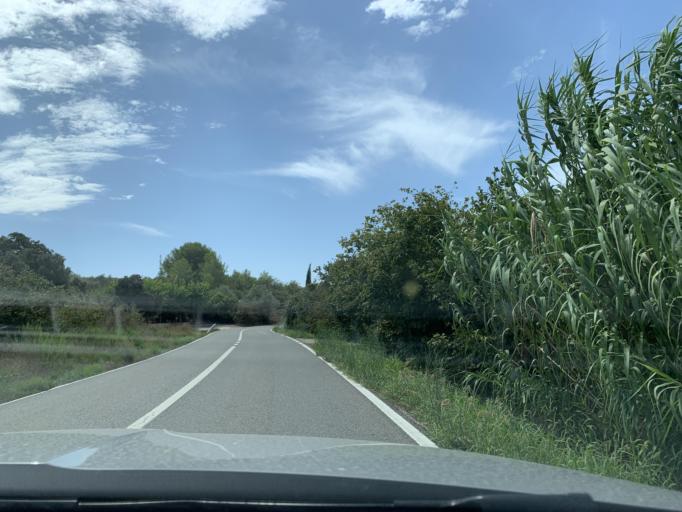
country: ES
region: Catalonia
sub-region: Provincia de Tarragona
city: Altafulla
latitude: 41.1648
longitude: 1.3674
